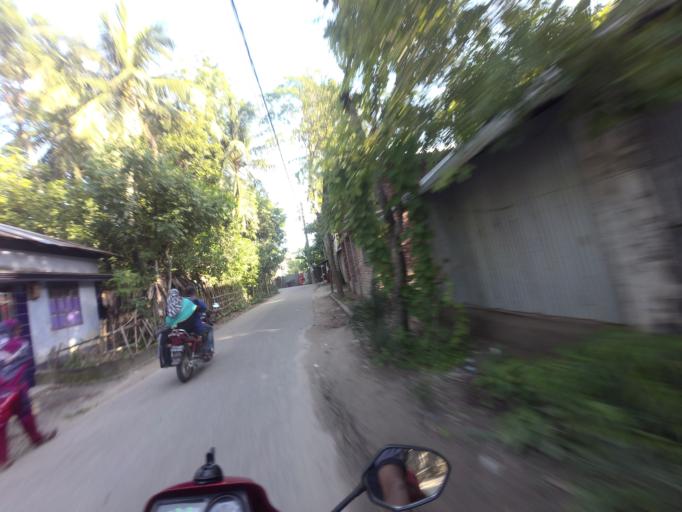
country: BD
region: Khulna
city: Khulna
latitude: 22.9213
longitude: 89.5176
